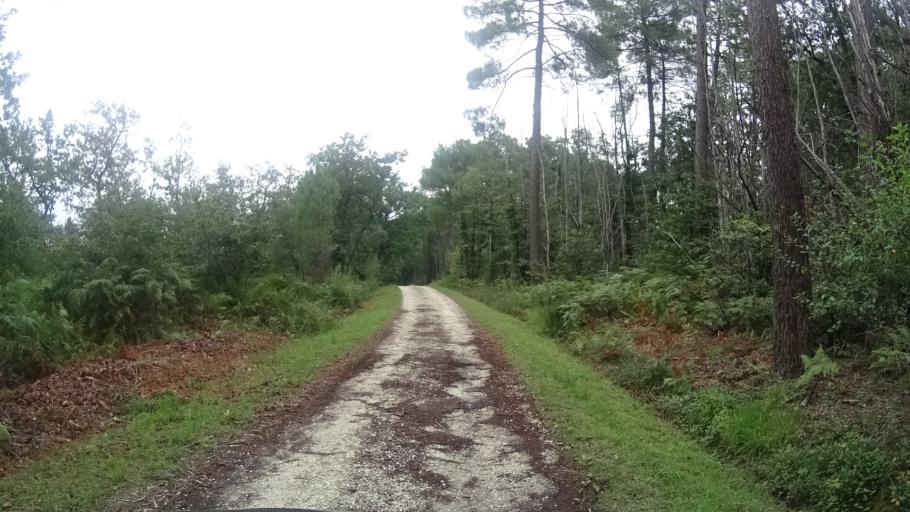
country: FR
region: Aquitaine
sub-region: Departement de la Dordogne
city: Sourzac
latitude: 45.0296
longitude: 0.4423
